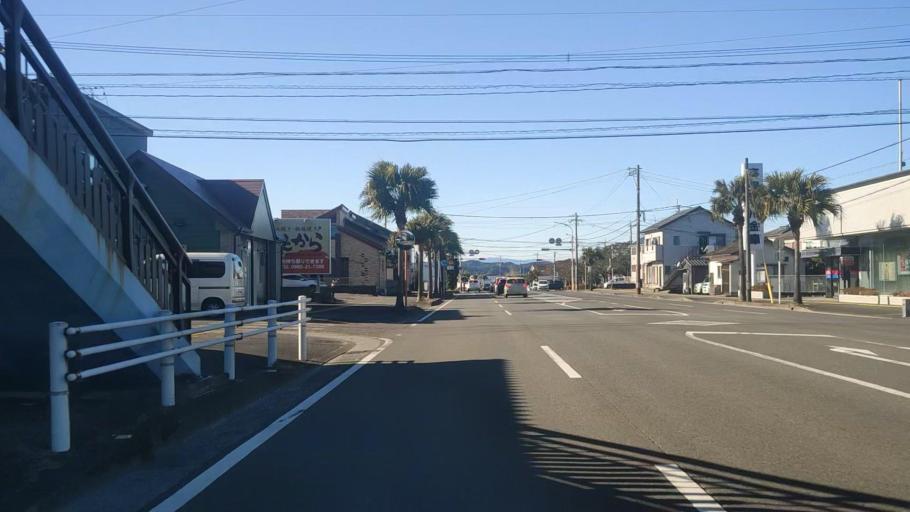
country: JP
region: Miyazaki
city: Miyazaki-shi
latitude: 31.9410
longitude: 131.4500
